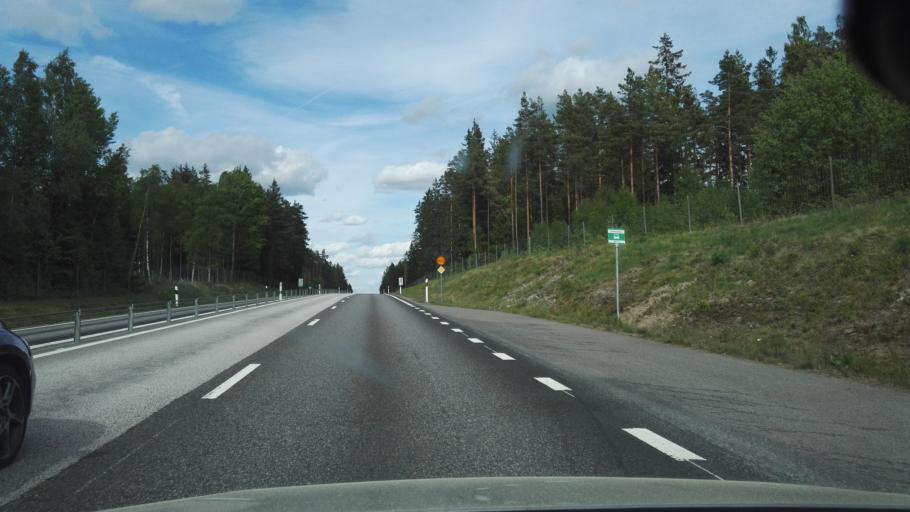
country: SE
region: Kronoberg
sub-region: Vaxjo Kommun
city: Rottne
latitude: 56.9544
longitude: 14.9358
